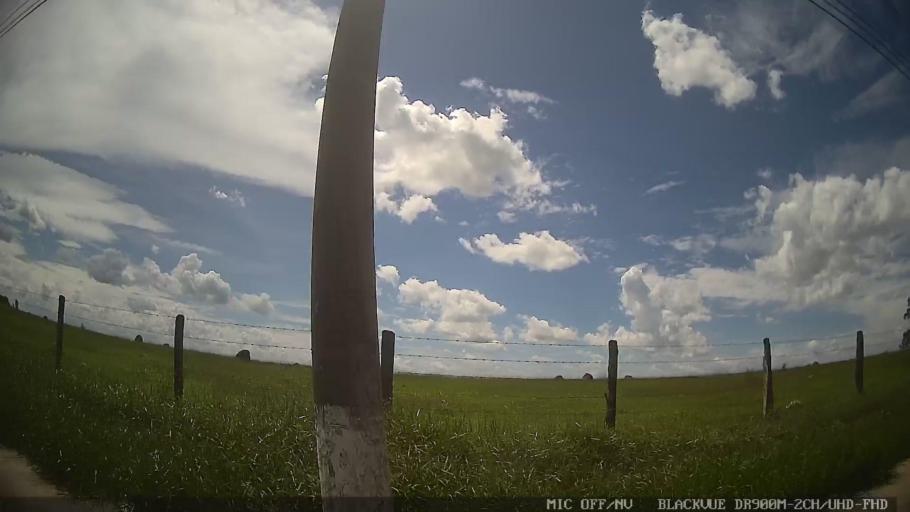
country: BR
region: Sao Paulo
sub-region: Conchas
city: Conchas
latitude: -23.0364
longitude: -48.0175
